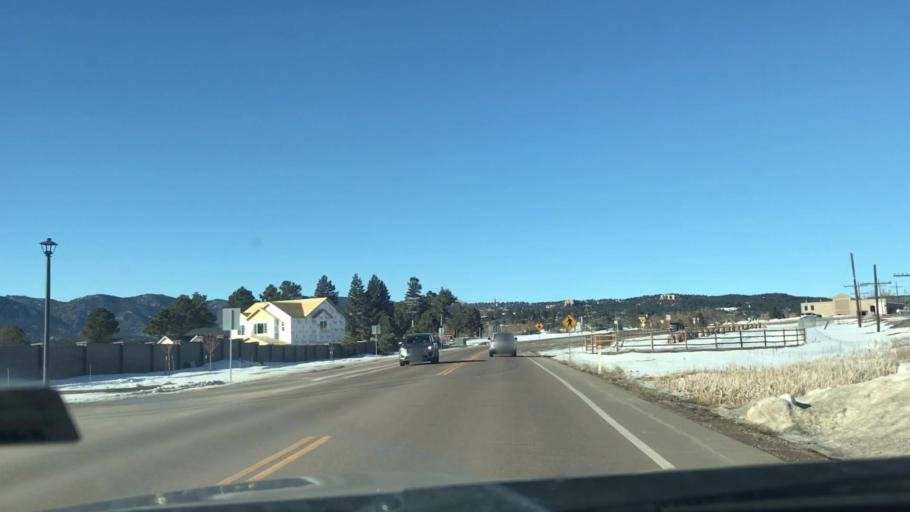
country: US
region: Colorado
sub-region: El Paso County
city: Monument
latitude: 39.0895
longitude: -104.8751
